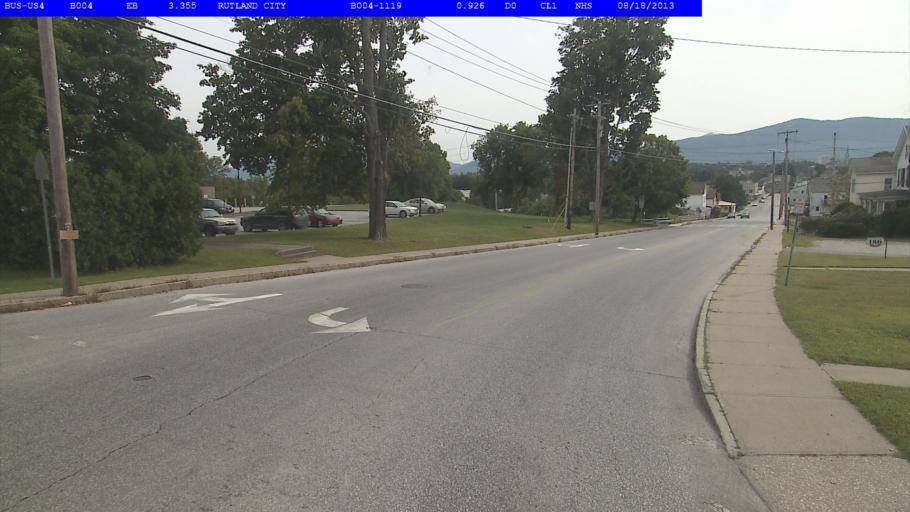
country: US
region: Vermont
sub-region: Rutland County
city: Rutland
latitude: 43.6083
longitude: -72.9907
